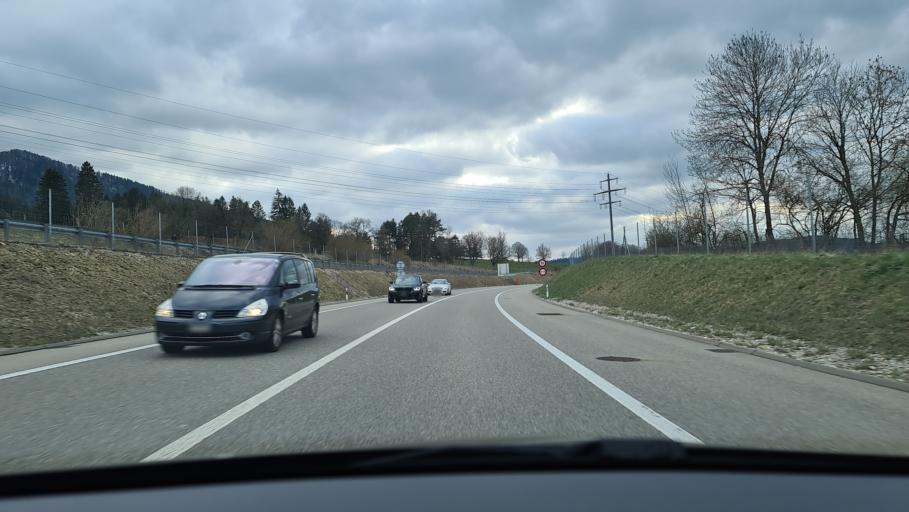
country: CH
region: Bern
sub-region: Jura bernois
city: Reconvilier
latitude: 47.2294
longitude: 7.2308
